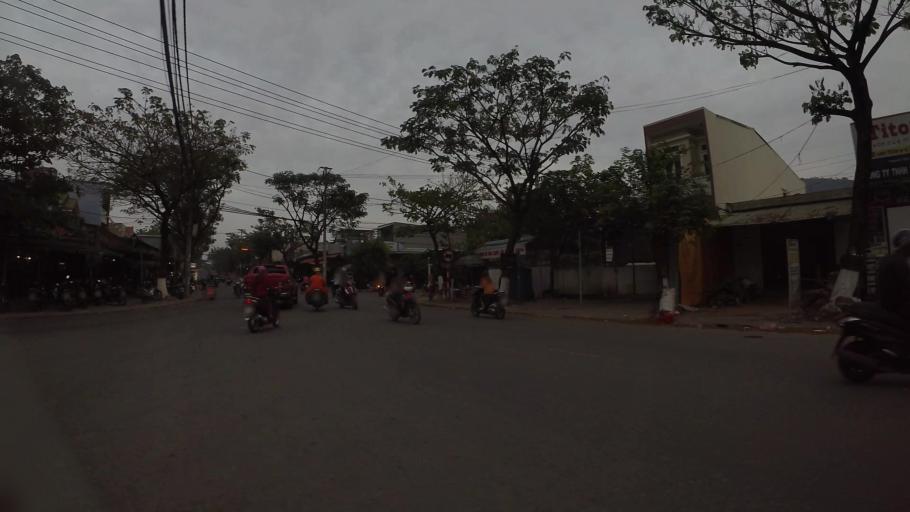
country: VN
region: Da Nang
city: Lien Chieu
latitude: 16.0779
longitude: 108.1213
